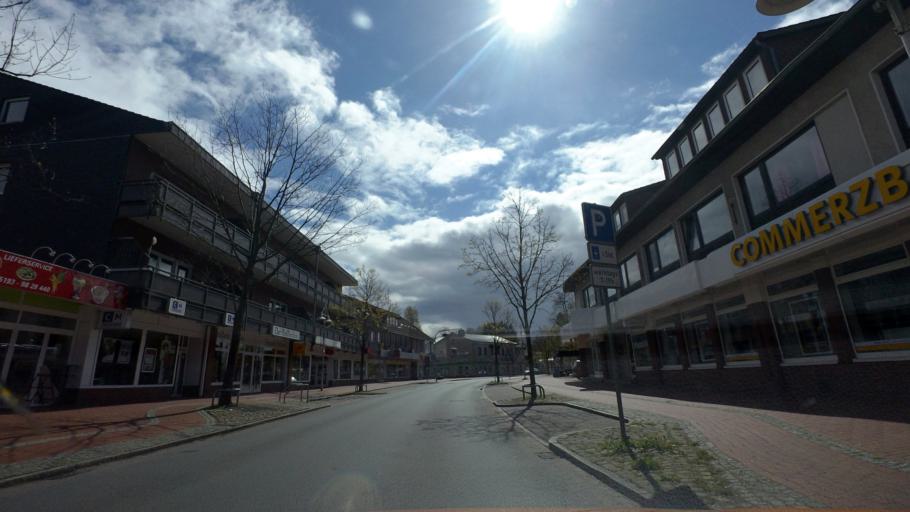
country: DE
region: Lower Saxony
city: Schneverdingen
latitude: 53.1176
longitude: 9.7884
